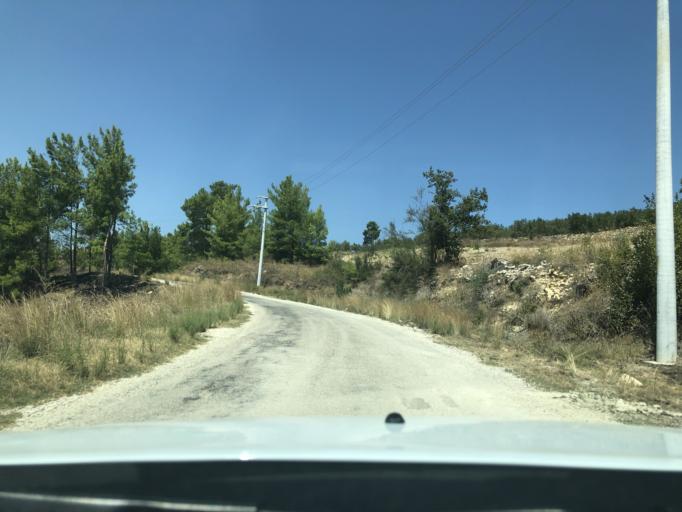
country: TR
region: Antalya
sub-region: Manavgat
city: Kizilagac
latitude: 36.8683
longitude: 31.5570
